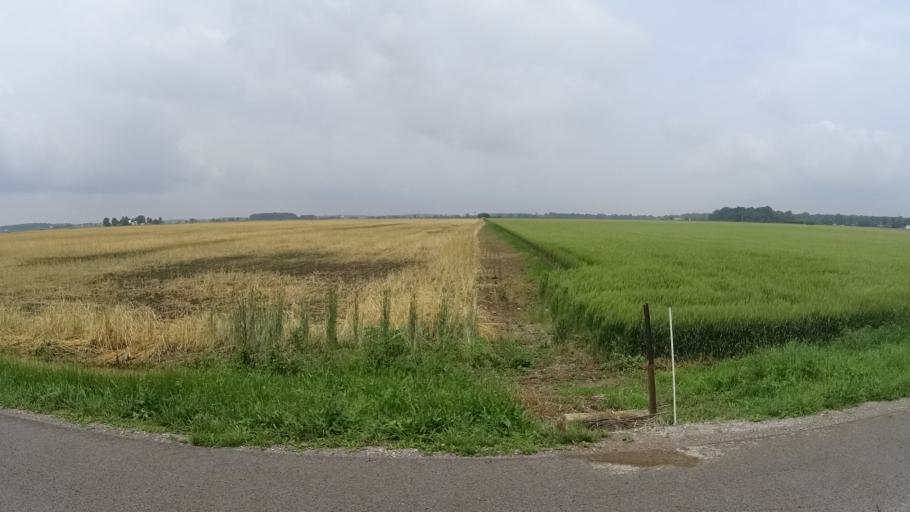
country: US
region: Ohio
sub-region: Huron County
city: Bellevue
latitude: 41.3190
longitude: -82.7930
